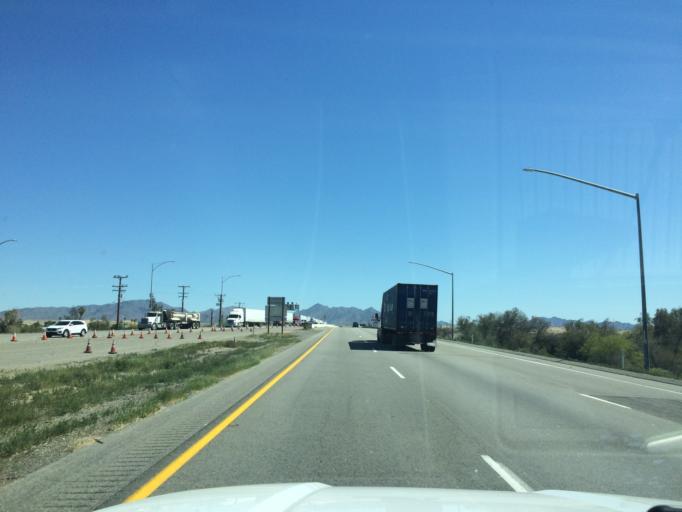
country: US
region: Arizona
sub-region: La Paz County
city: Ehrenberg
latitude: 33.6056
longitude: -114.5350
